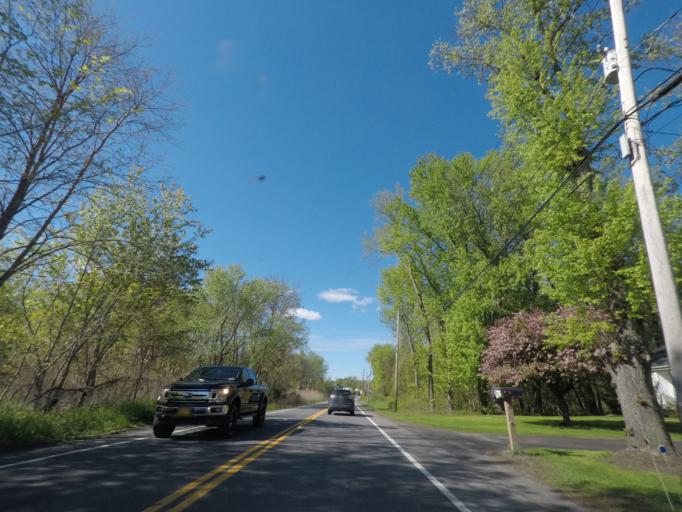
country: US
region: New York
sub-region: Albany County
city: Delmar
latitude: 42.5861
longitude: -73.7972
